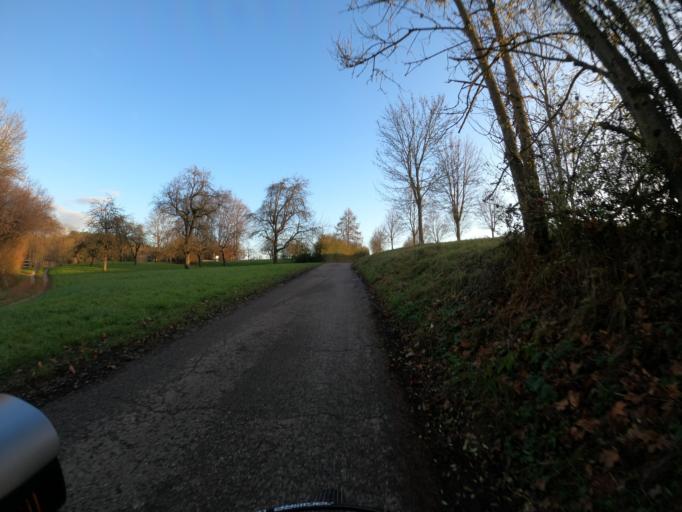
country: DE
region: Baden-Wuerttemberg
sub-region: Regierungsbezirk Stuttgart
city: Wernau
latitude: 48.6768
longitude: 9.4293
